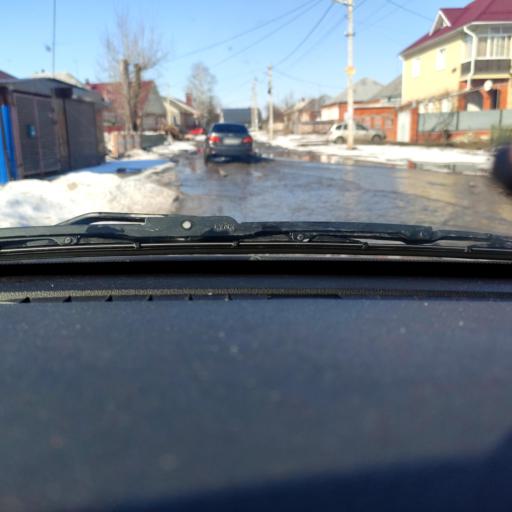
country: RU
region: Voronezj
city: Somovo
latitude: 51.7491
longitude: 39.3330
